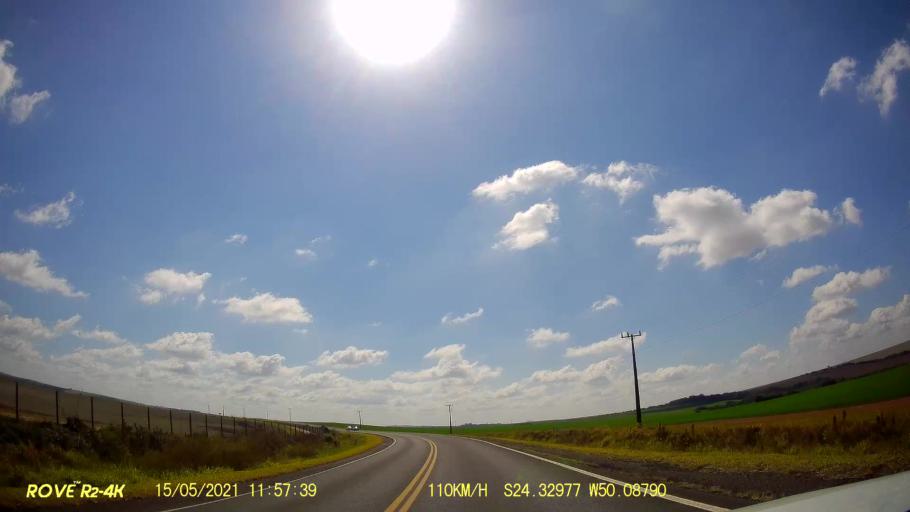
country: BR
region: Parana
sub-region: Pirai Do Sul
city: Pirai do Sul
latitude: -24.3309
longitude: -50.0889
